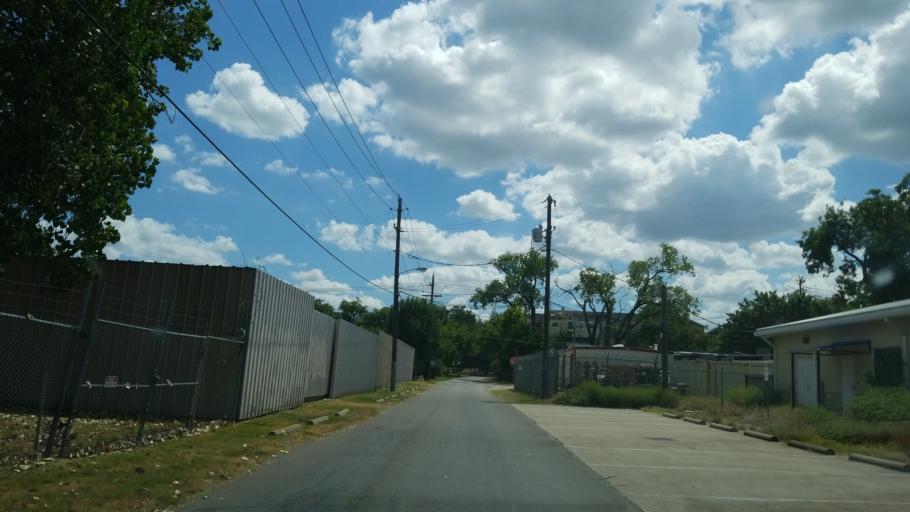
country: US
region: Texas
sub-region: Dallas County
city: Dallas
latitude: 32.7659
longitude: -96.8214
